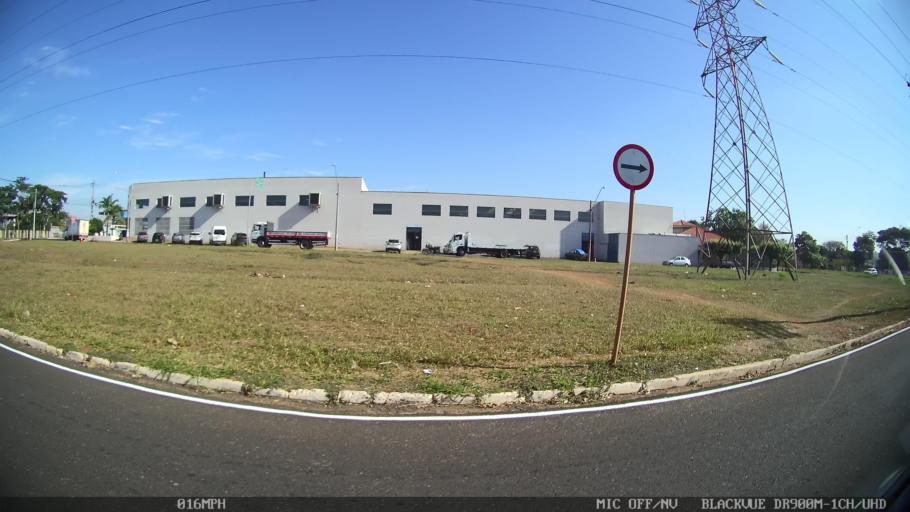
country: BR
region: Sao Paulo
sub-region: Sao Jose Do Rio Preto
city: Sao Jose do Rio Preto
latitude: -20.7929
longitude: -49.4148
